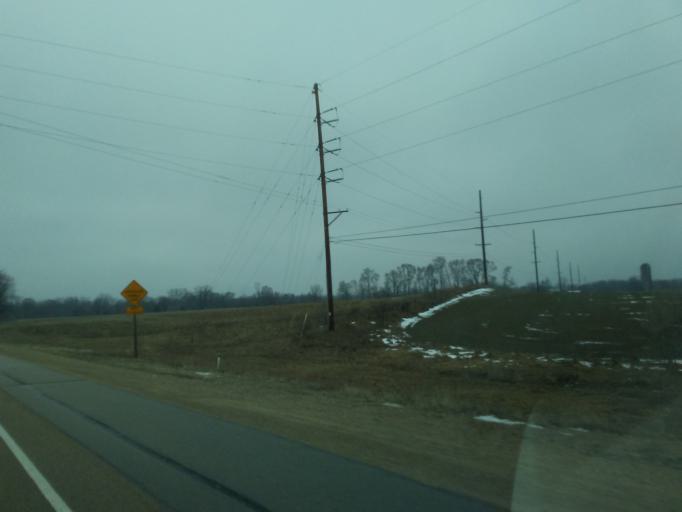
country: US
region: Wisconsin
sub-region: Dane County
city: Mazomanie
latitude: 43.1700
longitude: -89.7784
